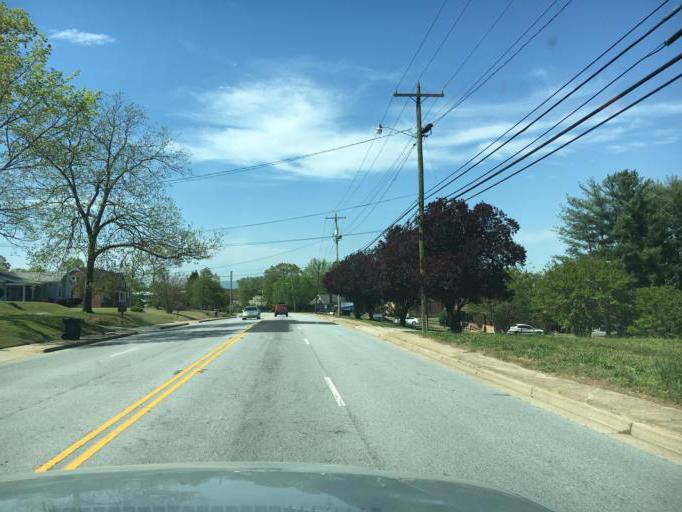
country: US
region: South Carolina
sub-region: Greenville County
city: Greer
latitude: 34.9511
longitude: -82.2256
